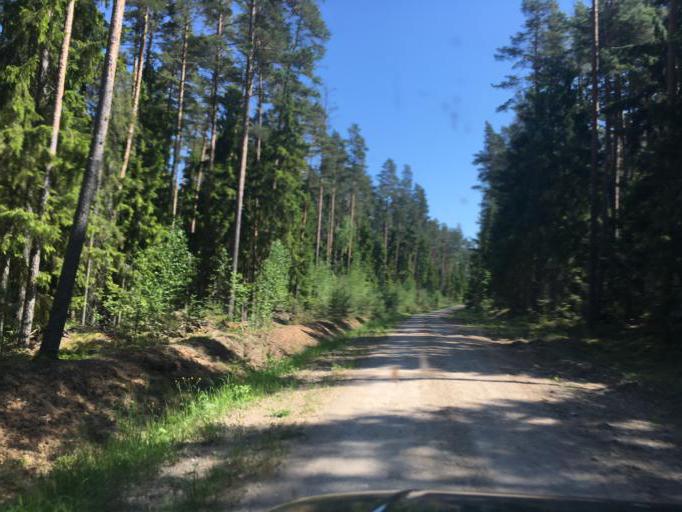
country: LV
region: Talsu Rajons
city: Valdemarpils
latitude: 57.4408
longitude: 22.6698
